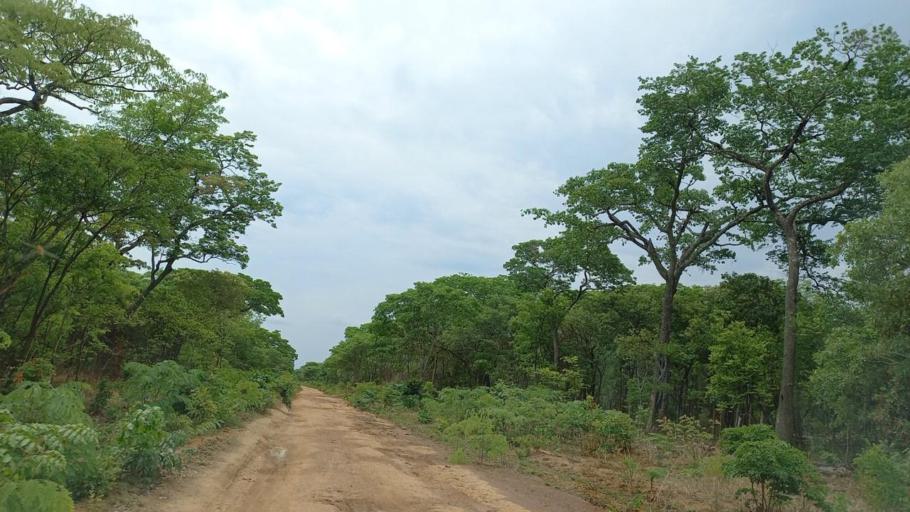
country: ZM
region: North-Western
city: Kalengwa
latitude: -13.5889
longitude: 24.9723
